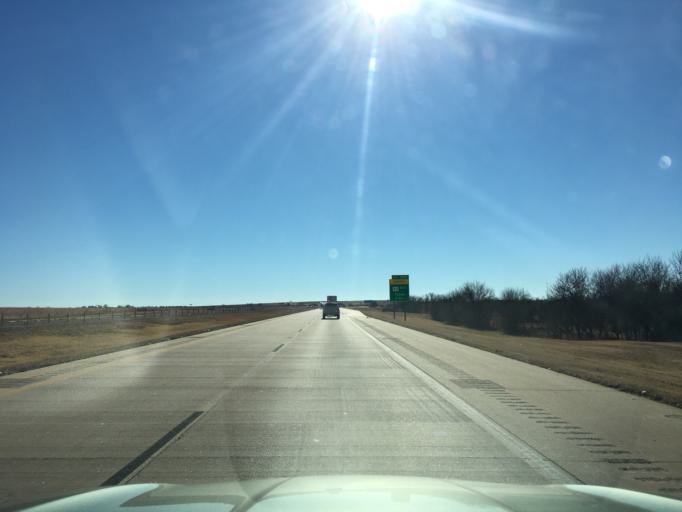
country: US
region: Oklahoma
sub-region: Noble County
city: Perry
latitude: 36.4199
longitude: -97.3271
